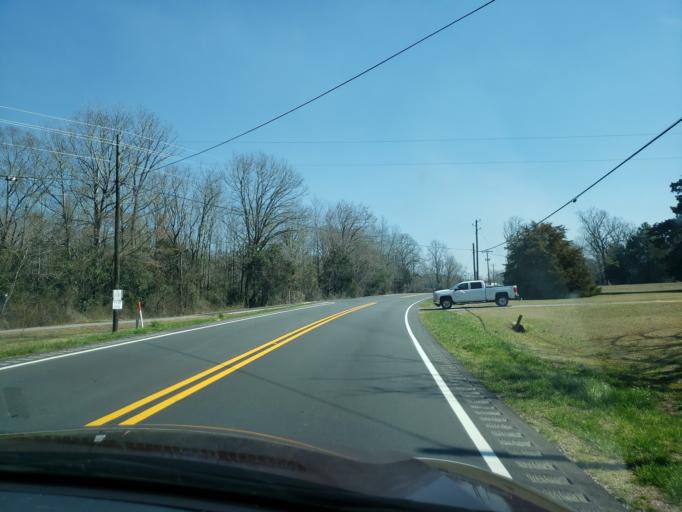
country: US
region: Alabama
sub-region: Macon County
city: Tuskegee
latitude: 32.5817
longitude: -85.7171
